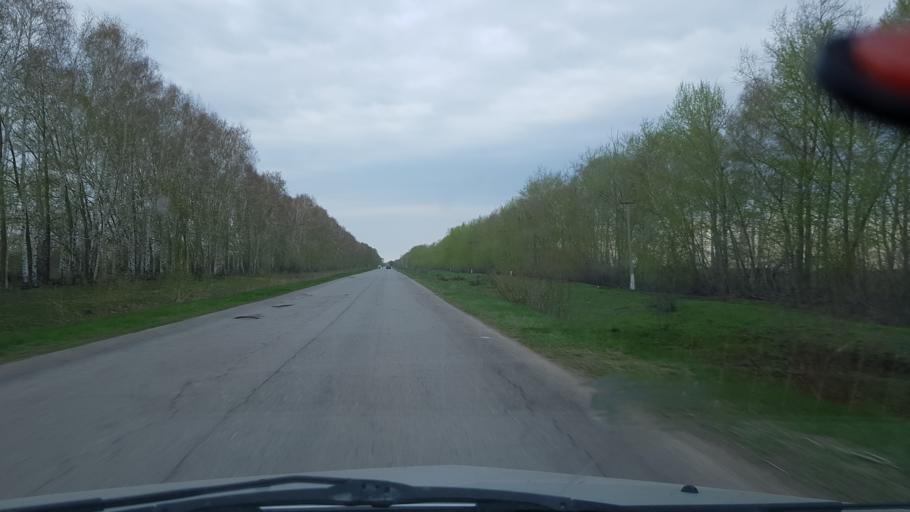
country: RU
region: Samara
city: Podstepki
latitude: 53.6628
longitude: 49.1968
